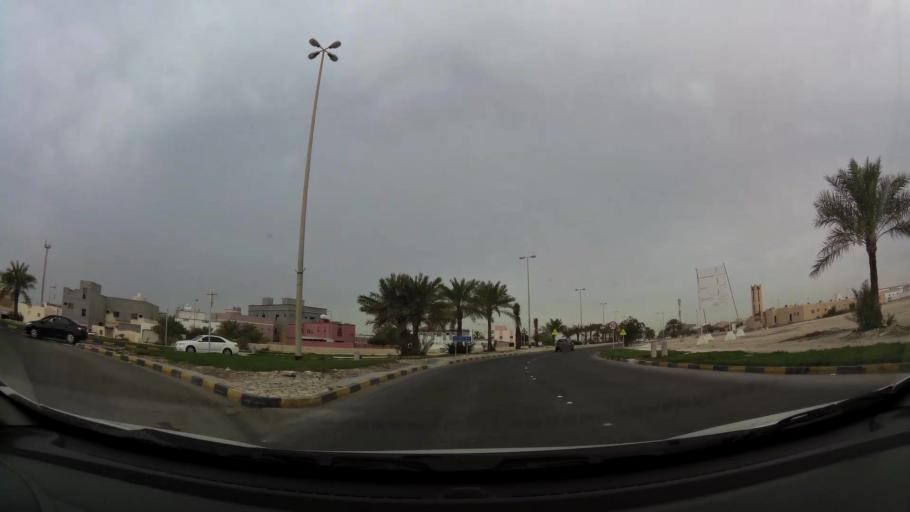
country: BH
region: Central Governorate
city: Dar Kulayb
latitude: 26.0688
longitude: 50.5079
